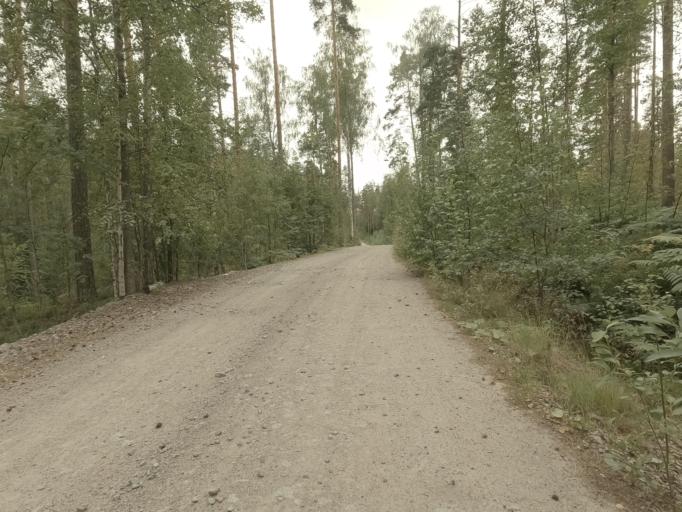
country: RU
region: Leningrad
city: Kamennogorsk
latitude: 60.9810
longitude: 29.1720
